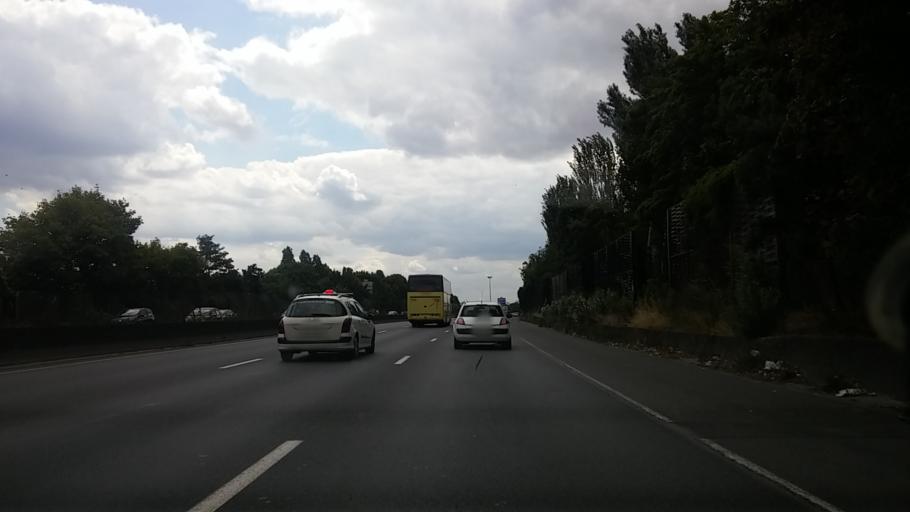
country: FR
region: Ile-de-France
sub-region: Departement de Seine-Saint-Denis
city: Bondy
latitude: 48.9119
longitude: 2.4760
